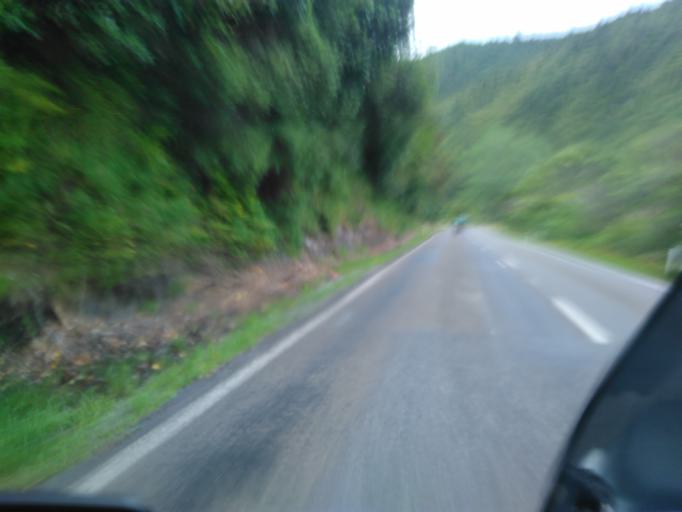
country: NZ
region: Bay of Plenty
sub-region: Opotiki District
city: Opotiki
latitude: -38.2443
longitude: 177.3069
